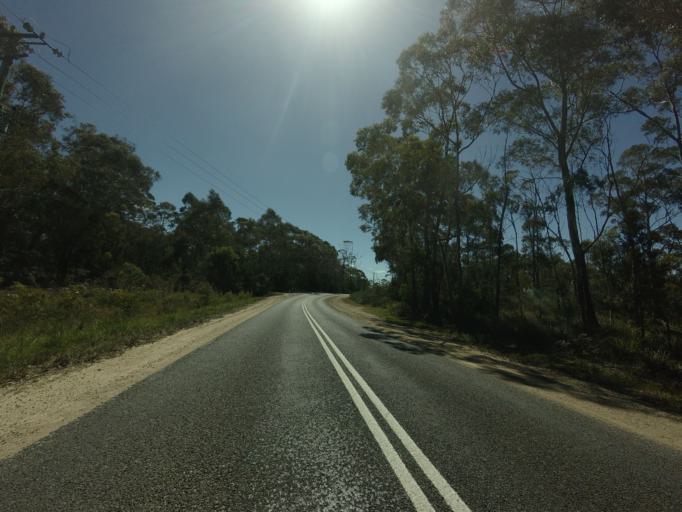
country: AU
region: Tasmania
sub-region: Break O'Day
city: St Helens
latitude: -41.8402
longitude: 148.2542
